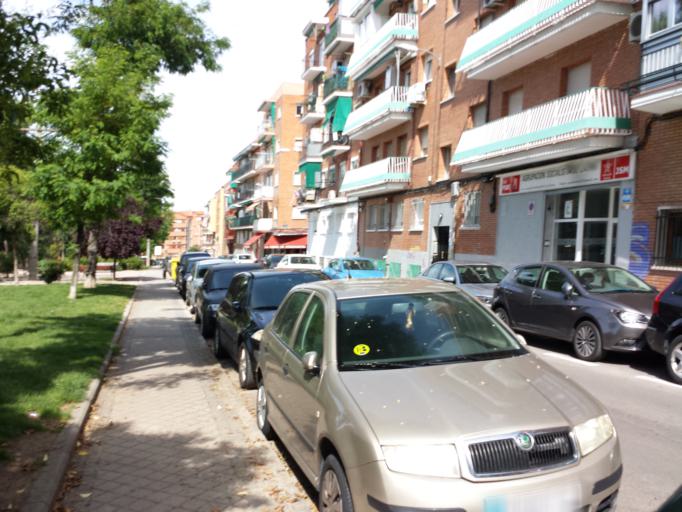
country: ES
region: Madrid
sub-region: Provincia de Madrid
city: Latina
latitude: 40.3918
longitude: -3.7455
